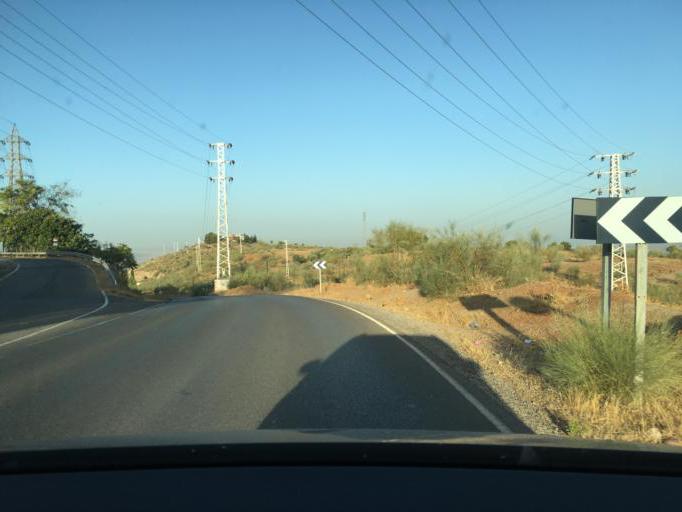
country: ES
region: Andalusia
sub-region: Provincia de Granada
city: Jun
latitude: 37.1971
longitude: -3.5765
